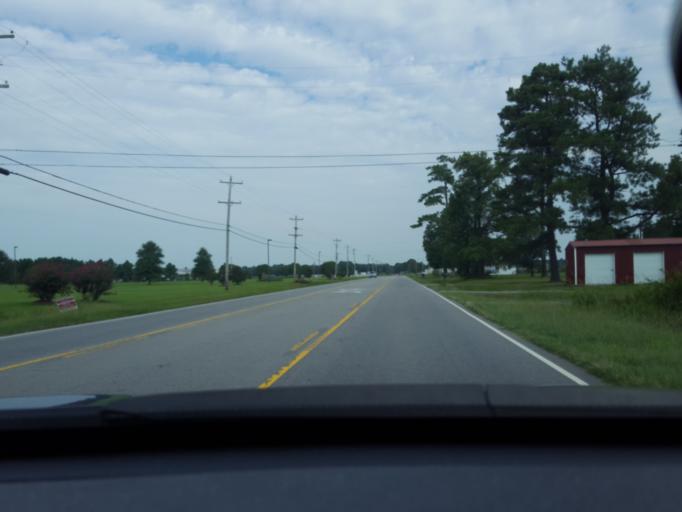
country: US
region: North Carolina
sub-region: Chowan County
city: Edenton
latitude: 36.0877
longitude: -76.6297
